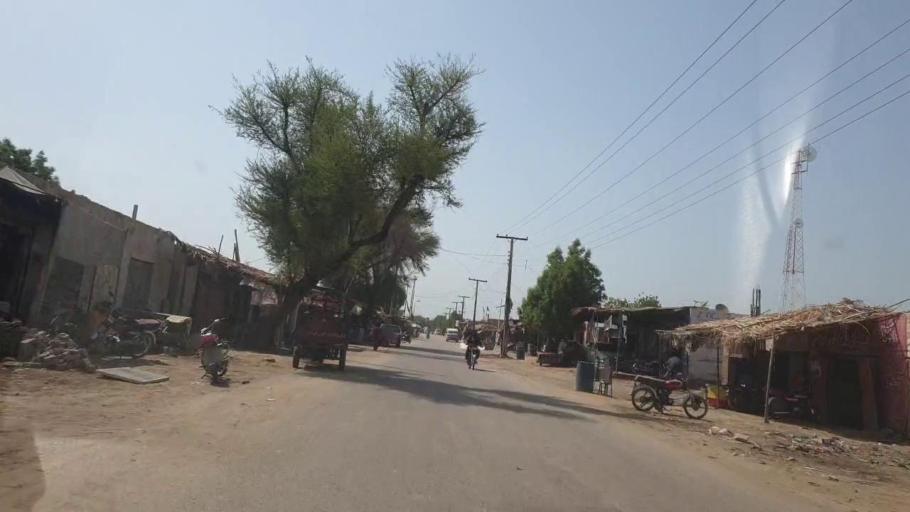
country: PK
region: Sindh
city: Setharja Old
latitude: 27.1302
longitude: 68.5347
